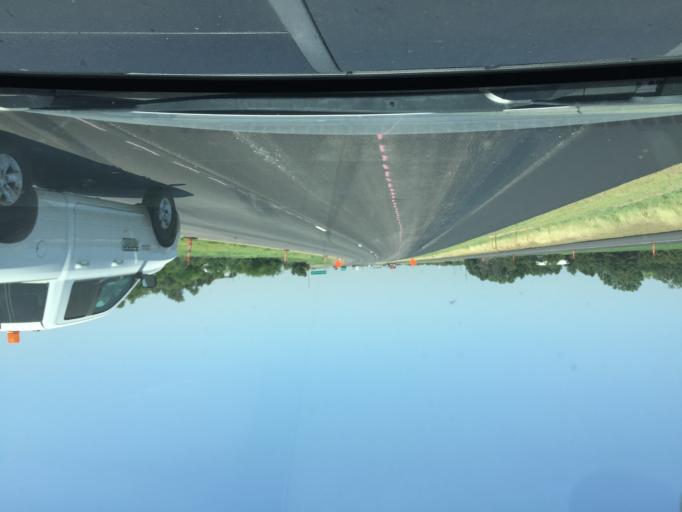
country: US
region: Kansas
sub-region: Reno County
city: South Hutchinson
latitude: 38.0139
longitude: -97.9990
